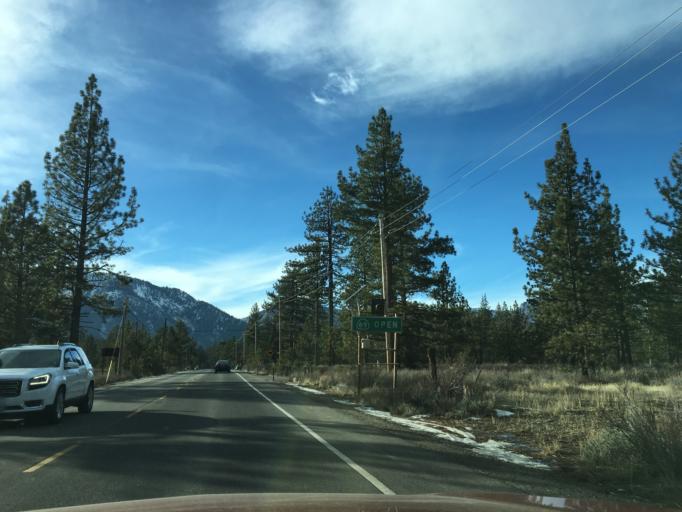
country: US
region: California
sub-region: El Dorado County
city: South Lake Tahoe
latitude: 38.9342
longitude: -120.0459
